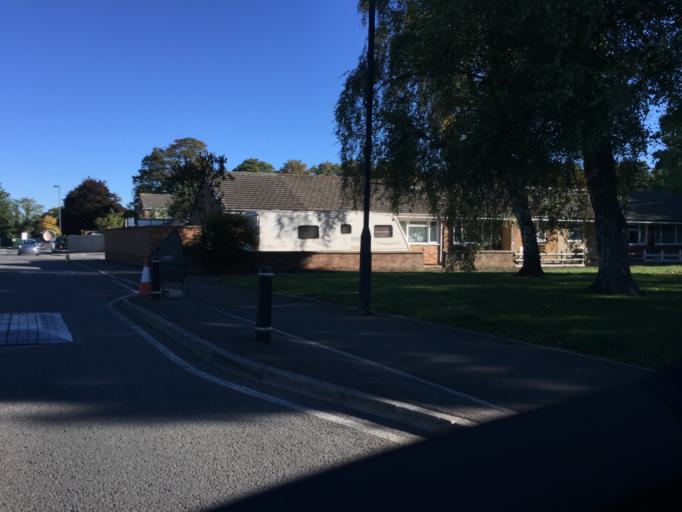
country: GB
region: England
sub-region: South Gloucestershire
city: Yate
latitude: 51.5346
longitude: -2.4165
